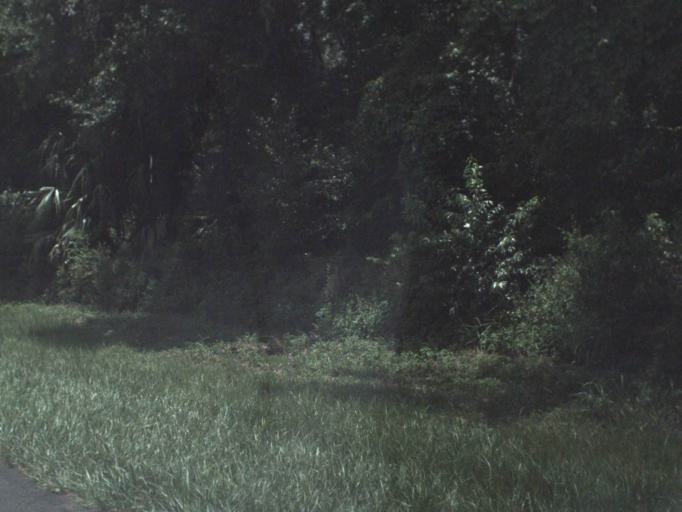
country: US
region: Florida
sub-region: Levy County
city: Williston
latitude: 29.4263
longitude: -82.4577
